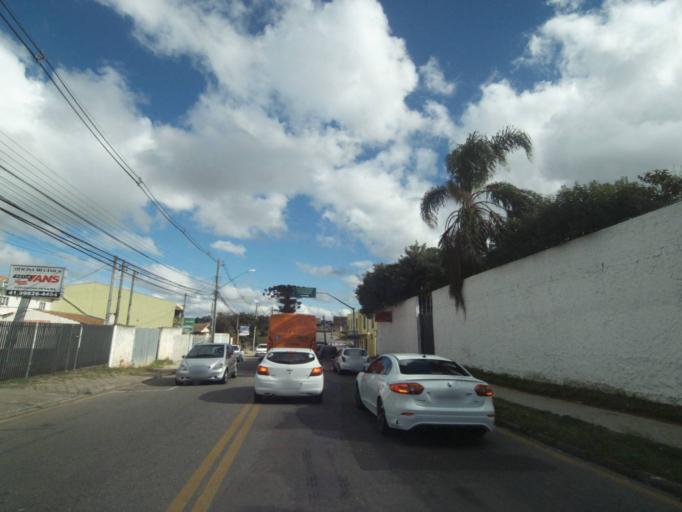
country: BR
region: Parana
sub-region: Sao Jose Dos Pinhais
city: Sao Jose dos Pinhais
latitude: -25.5231
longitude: -49.2929
